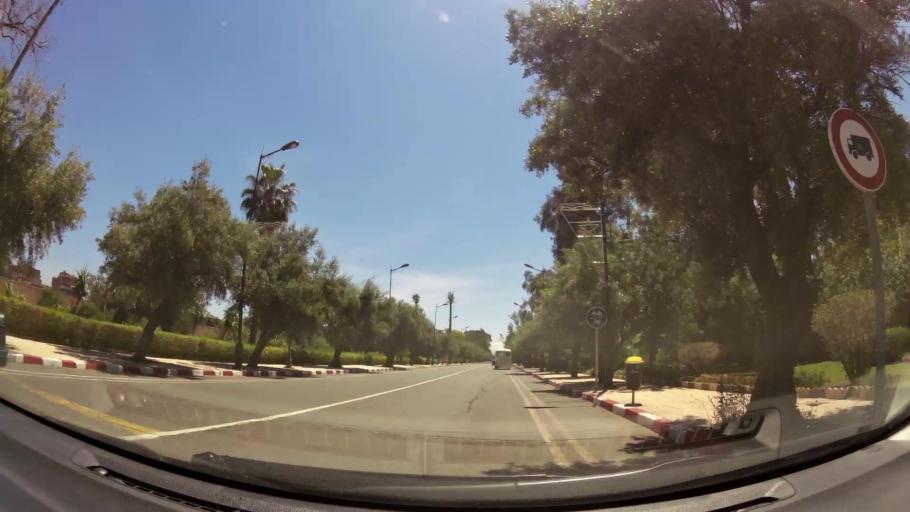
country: MA
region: Marrakech-Tensift-Al Haouz
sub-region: Marrakech
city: Marrakesh
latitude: 31.6258
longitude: -8.0097
